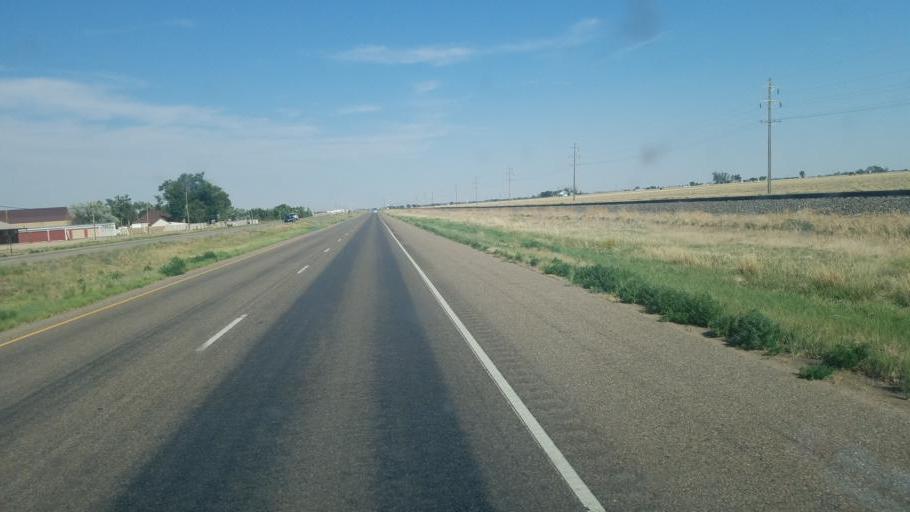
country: US
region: Colorado
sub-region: Otero County
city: Rocky Ford
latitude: 38.0378
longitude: -103.6822
